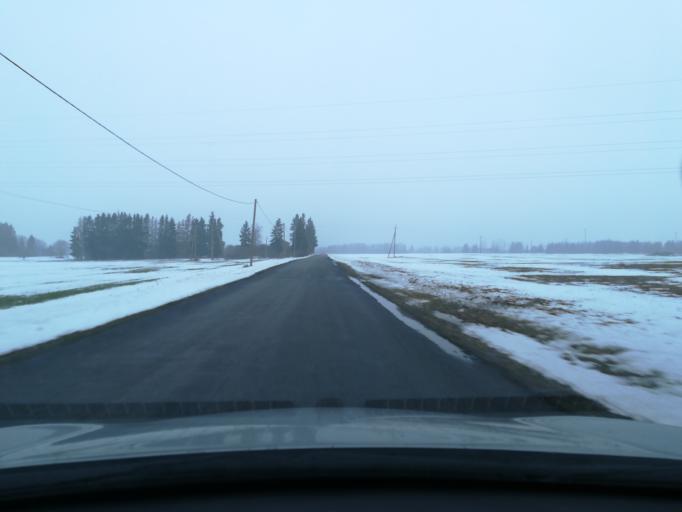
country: EE
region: Harju
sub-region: Raasiku vald
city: Raasiku
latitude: 59.3585
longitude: 25.1990
